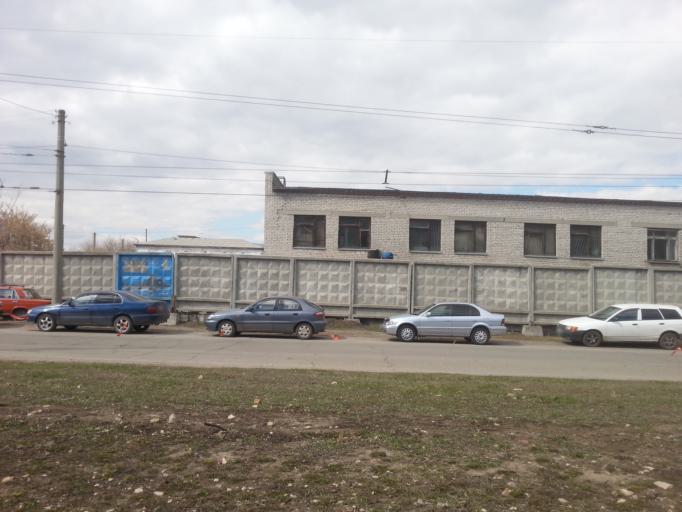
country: RU
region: Altai Krai
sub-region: Gorod Barnaulskiy
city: Barnaul
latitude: 53.3853
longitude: 83.7105
